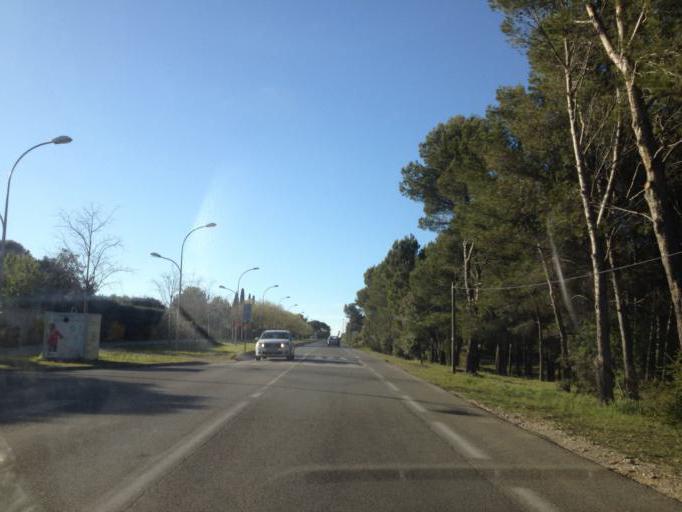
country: FR
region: Provence-Alpes-Cote d'Azur
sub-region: Departement des Bouches-du-Rhone
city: Lambesc
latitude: 43.6454
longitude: 5.2687
